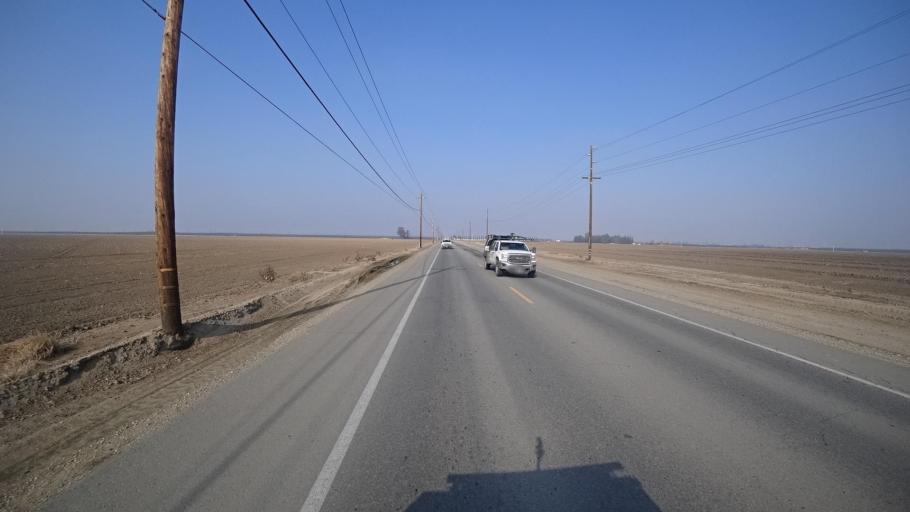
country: US
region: California
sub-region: Kern County
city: Greenfield
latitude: 35.2024
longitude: -119.1100
